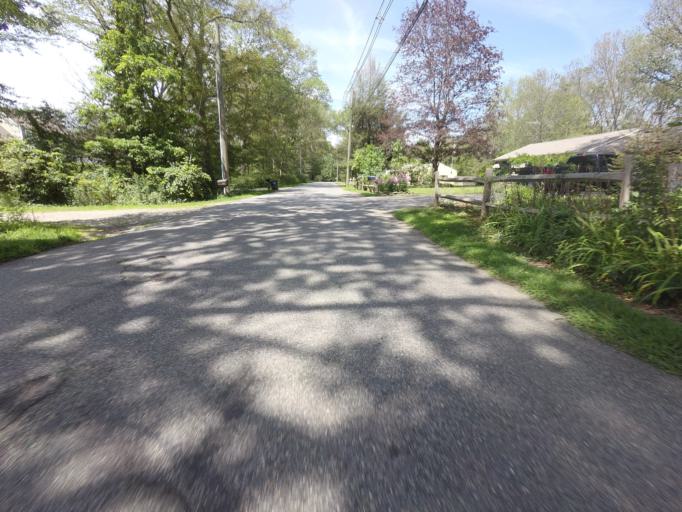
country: US
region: Connecticut
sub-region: Windham County
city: East Brooklyn
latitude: 41.8224
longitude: -71.9296
